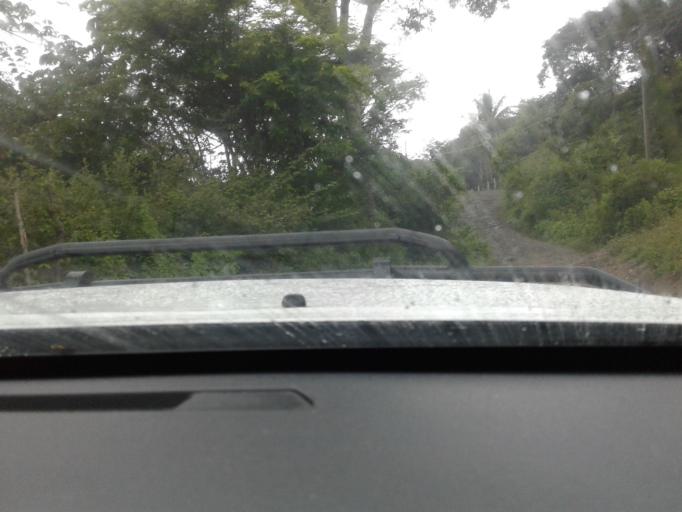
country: NI
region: Leon
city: Santa Rosa del Penon
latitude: 12.9025
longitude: -86.2391
